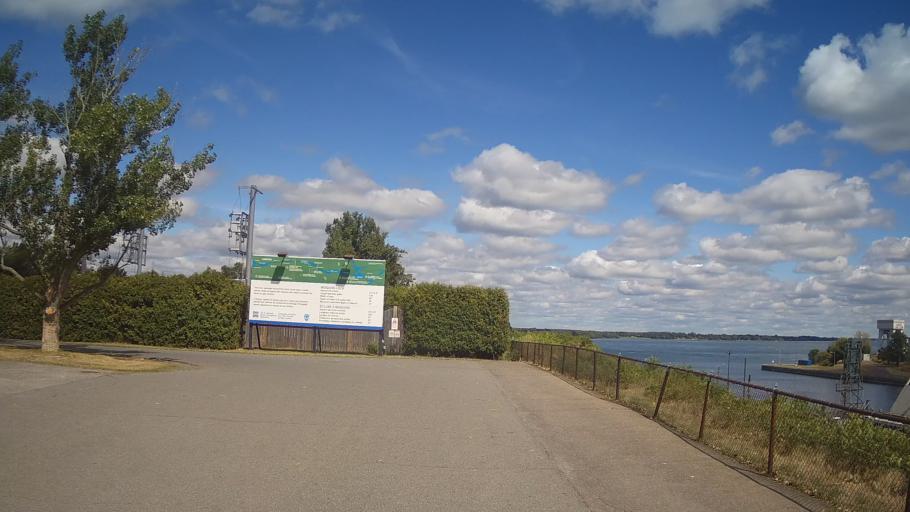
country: US
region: New York
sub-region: St. Lawrence County
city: Ogdensburg
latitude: 44.8321
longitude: -75.3131
